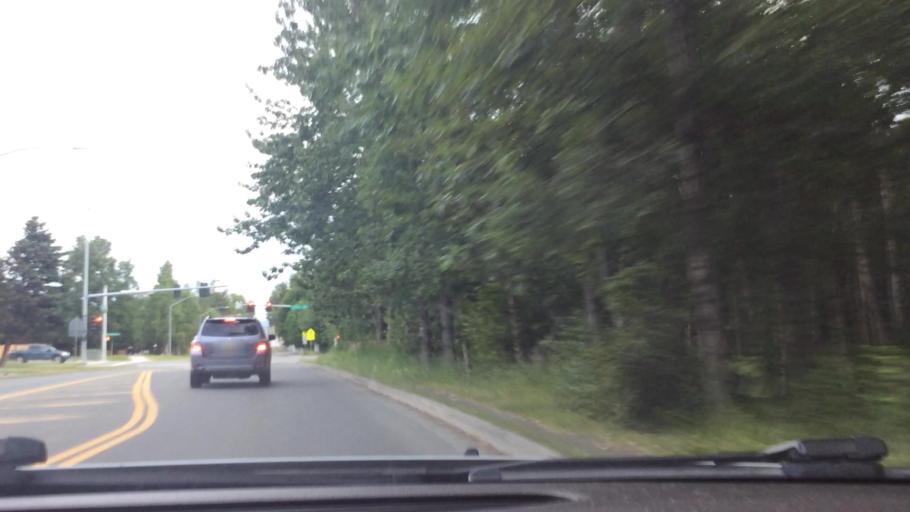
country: US
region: Alaska
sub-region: Anchorage Municipality
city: Anchorage
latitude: 61.1962
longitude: -149.7635
